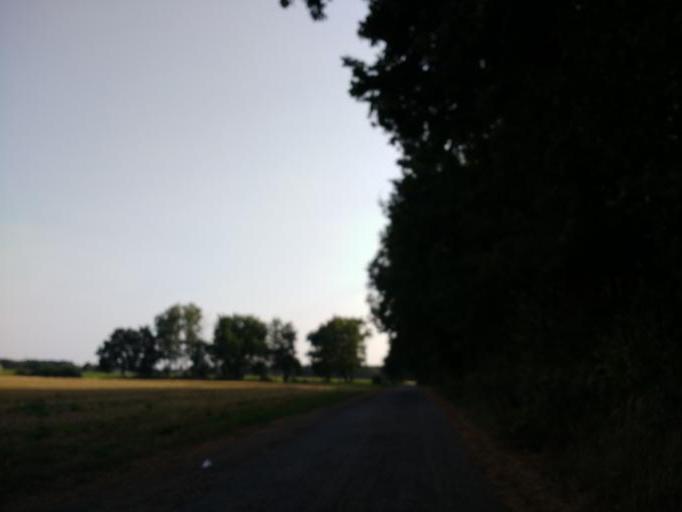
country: DE
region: Lower Saxony
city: Wagenhoff
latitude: 52.5072
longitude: 10.5185
